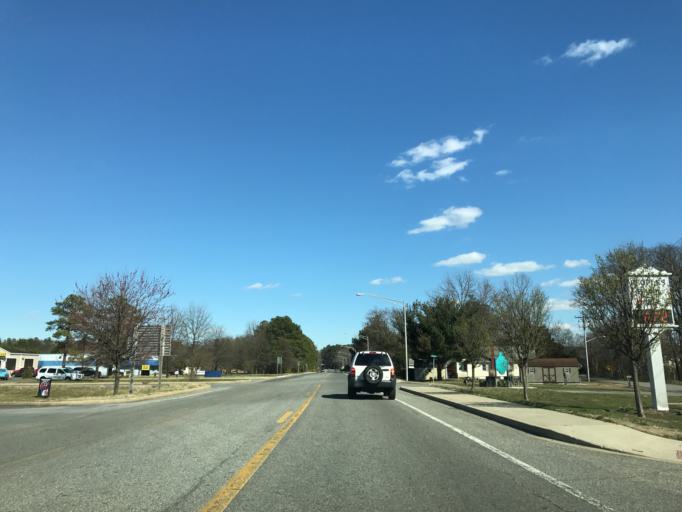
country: US
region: Maryland
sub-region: Kent County
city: Rock Hall
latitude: 39.1385
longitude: -76.2337
